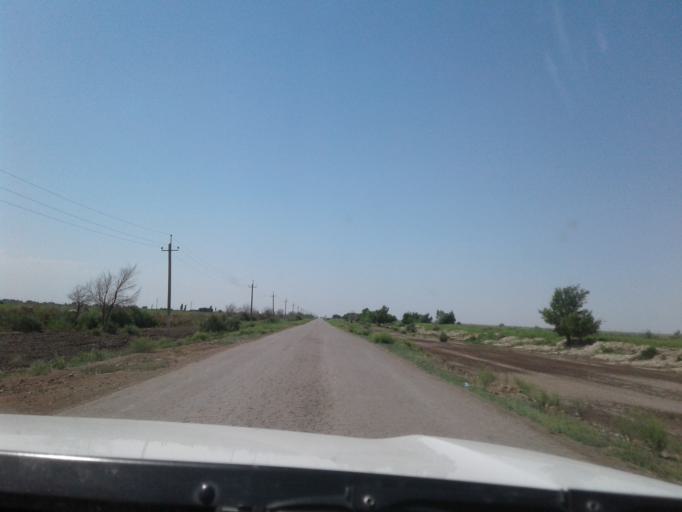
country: TM
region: Dasoguz
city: Koeneuergench
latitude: 41.8585
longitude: 58.7054
